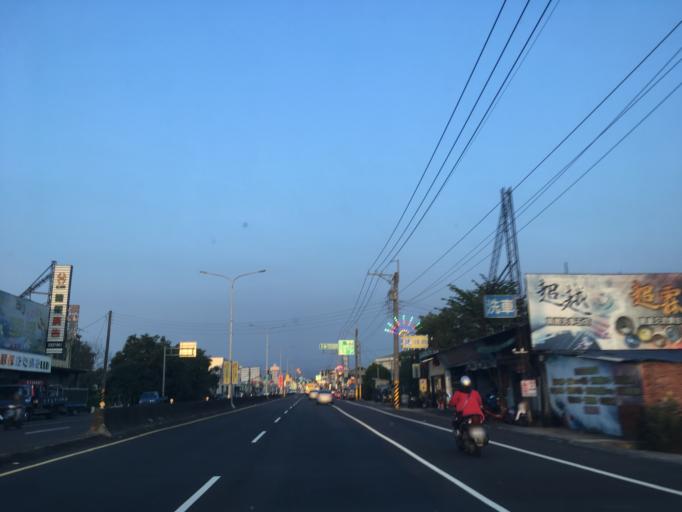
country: TW
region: Taiwan
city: Zhongxing New Village
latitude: 23.9875
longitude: 120.6755
